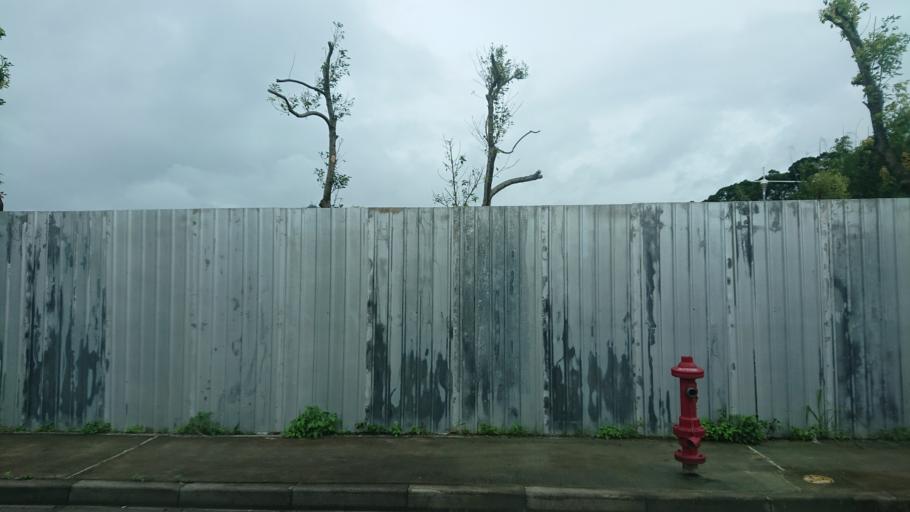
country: TW
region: Taipei
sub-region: Taipei
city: Banqiao
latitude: 24.9793
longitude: 121.4536
